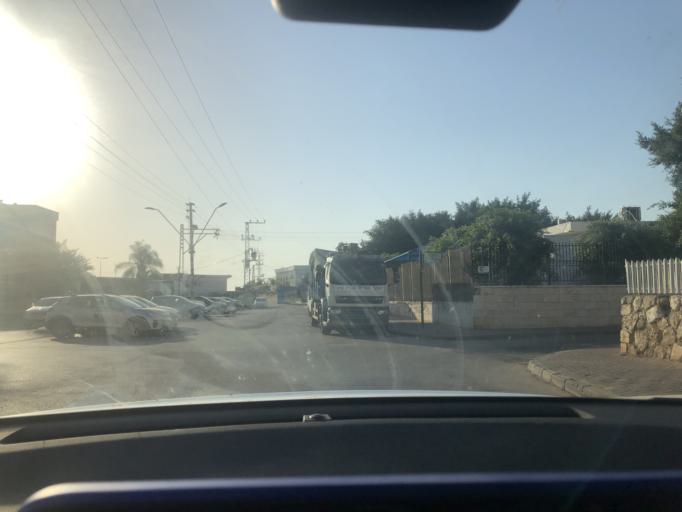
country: IL
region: Central District
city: Lod
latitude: 31.9518
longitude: 34.8871
